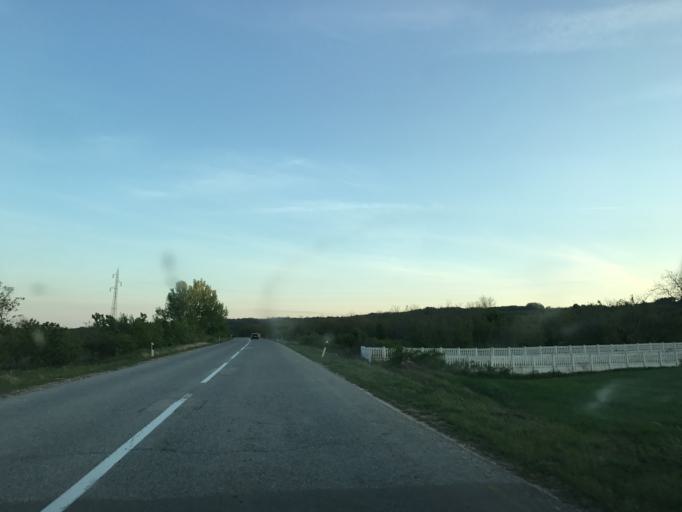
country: RO
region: Mehedinti
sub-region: Comuna Gogosu
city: Ostrovu Mare
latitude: 44.3437
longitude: 22.4742
